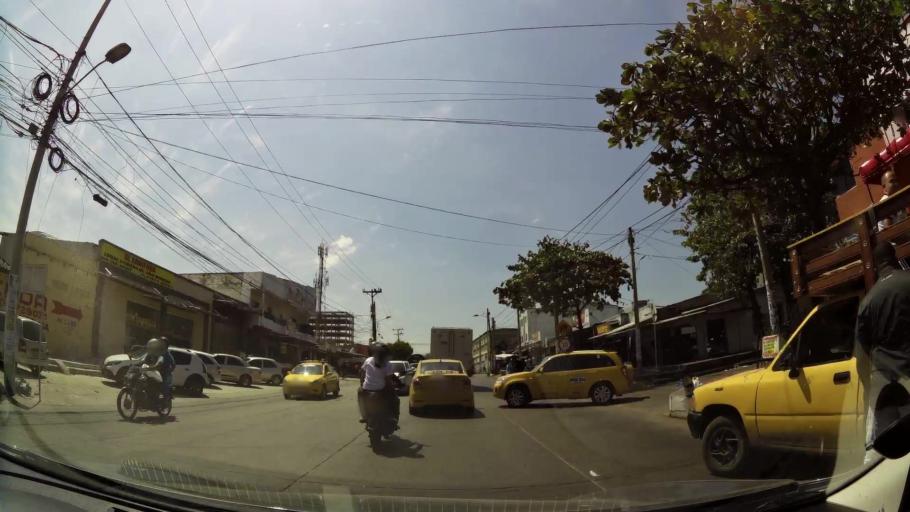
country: CO
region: Atlantico
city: Barranquilla
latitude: 10.9580
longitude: -74.8043
